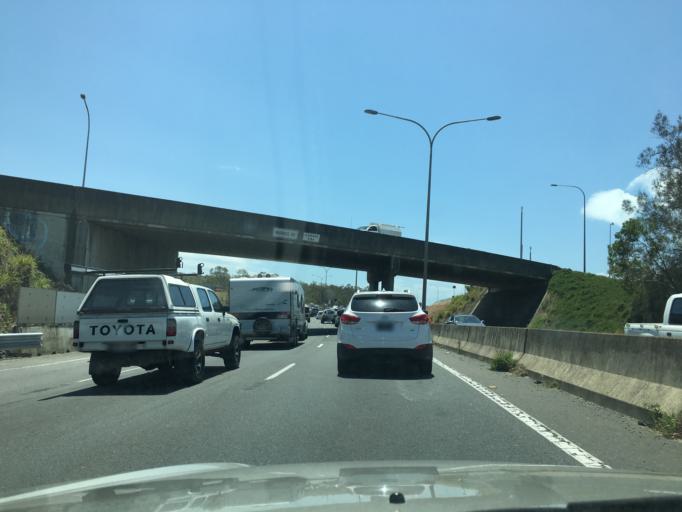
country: AU
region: Queensland
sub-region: Brisbane
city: Shorncliffe
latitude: -27.3745
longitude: 153.0967
